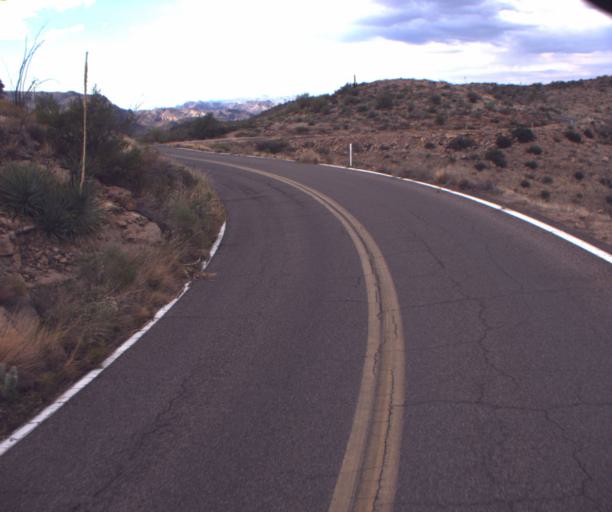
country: US
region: Arizona
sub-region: Pinal County
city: Gold Camp
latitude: 33.5420
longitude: -111.3281
